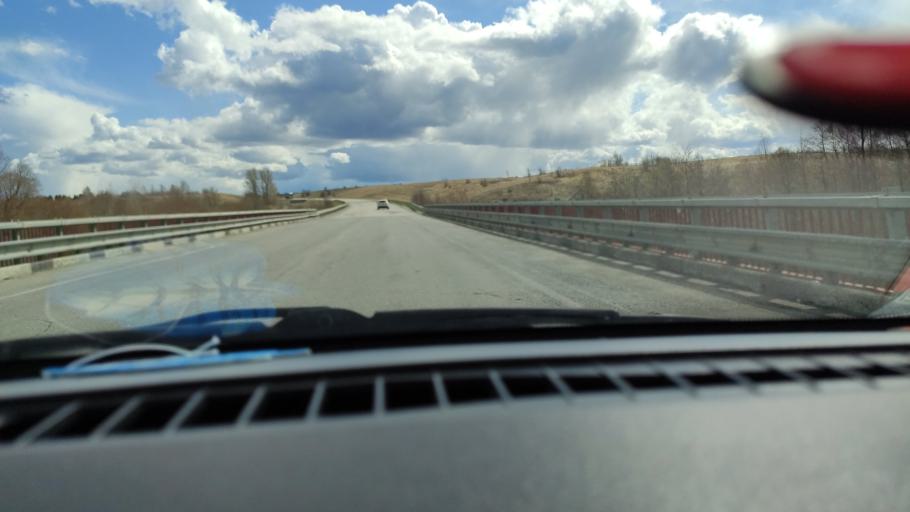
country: RU
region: Samara
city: Varlamovo
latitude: 53.1283
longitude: 48.2890
